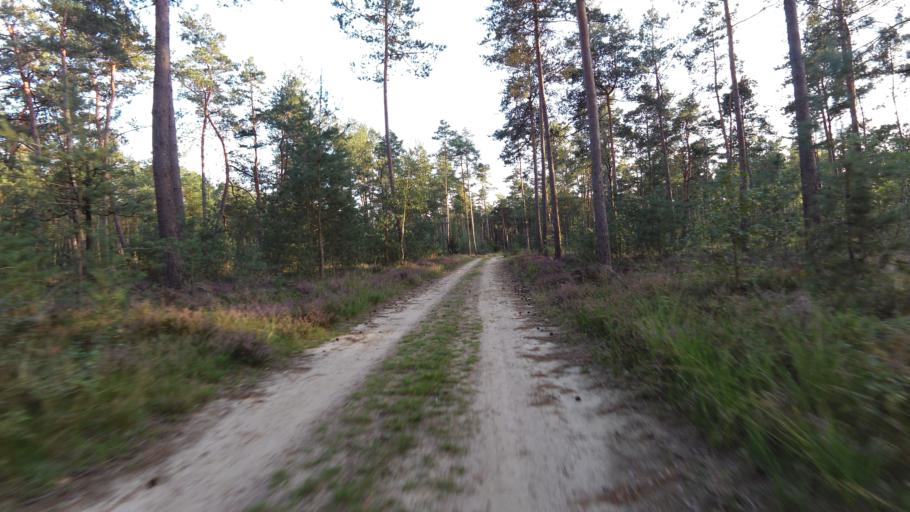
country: NL
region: Gelderland
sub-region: Gemeente Epe
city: Vaassen
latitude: 52.2822
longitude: 5.8901
